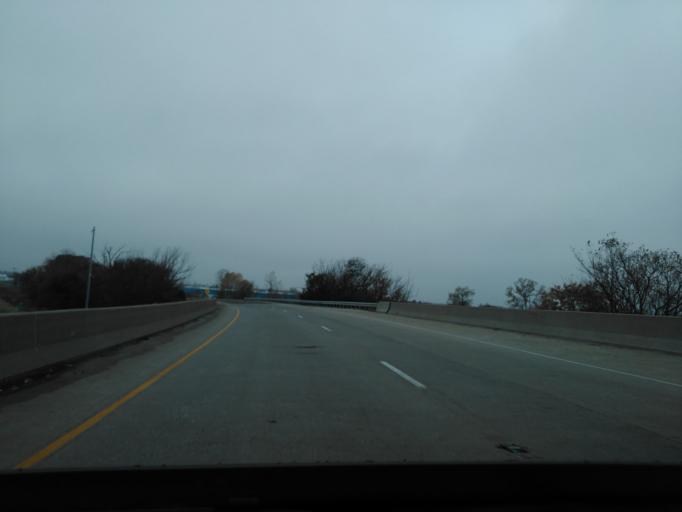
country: US
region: Illinois
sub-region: Madison County
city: Troy
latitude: 38.7487
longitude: -89.9082
